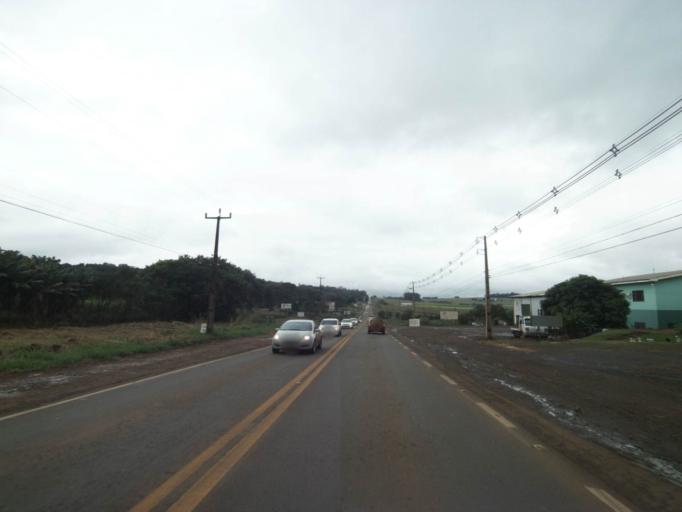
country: BR
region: Parana
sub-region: Marechal Candido Rondon
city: Marechal Candido Rondon
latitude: -24.5683
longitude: -54.0244
